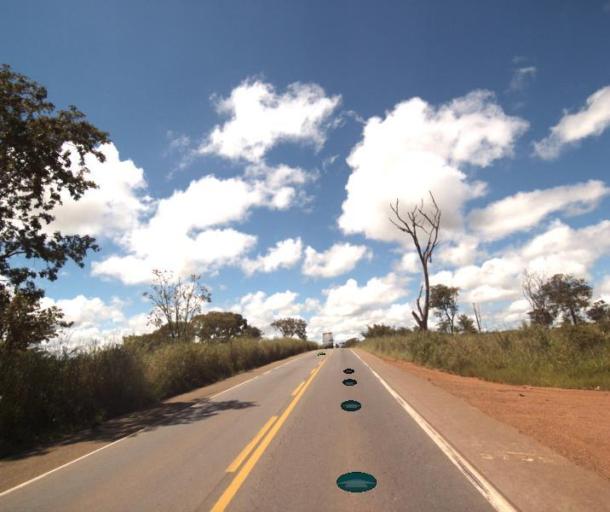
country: BR
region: Goias
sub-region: Jaragua
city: Jaragua
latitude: -15.8672
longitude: -49.2562
